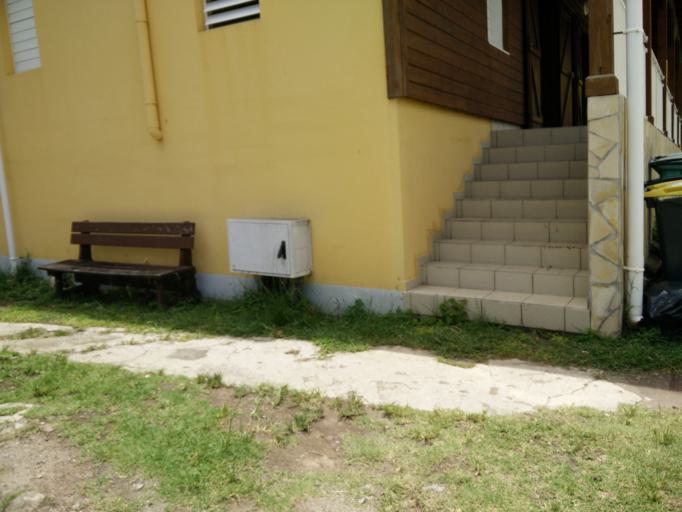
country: GP
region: Guadeloupe
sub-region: Guadeloupe
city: Terre-de-Bas
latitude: 15.8578
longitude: -61.6243
